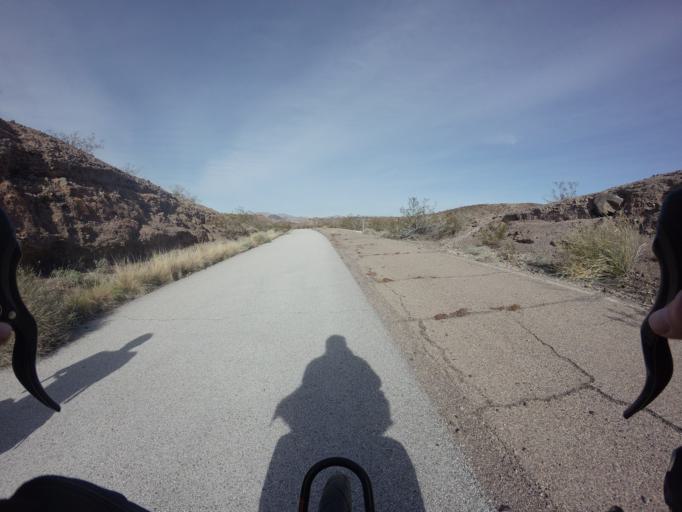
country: US
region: Nevada
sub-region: Clark County
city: Boulder City
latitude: 36.0879
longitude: -114.8339
